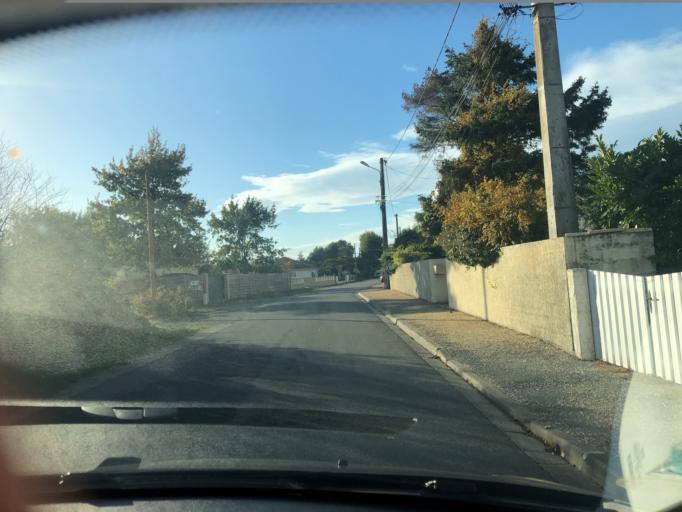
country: FR
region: Aquitaine
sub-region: Departement de la Gironde
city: Hourtin
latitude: 45.1833
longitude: -1.0530
